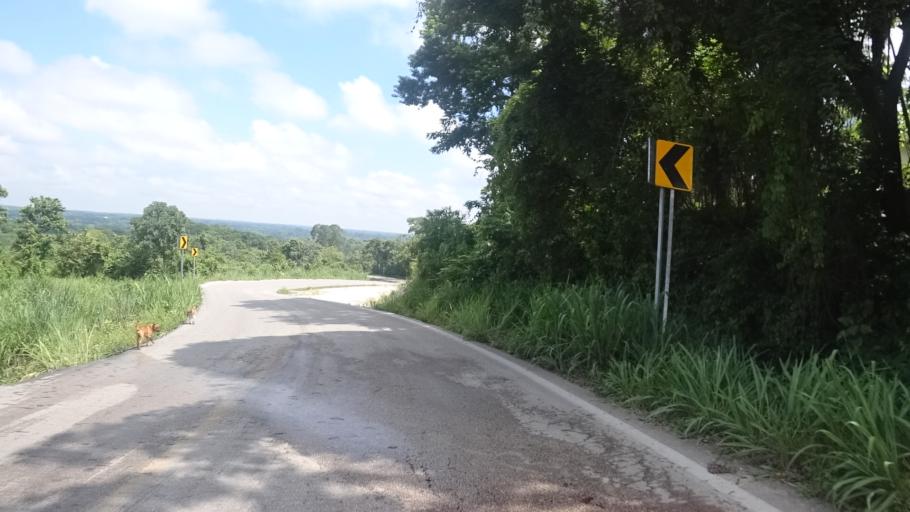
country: MX
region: Chiapas
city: Palenque
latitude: 17.4748
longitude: -91.9664
